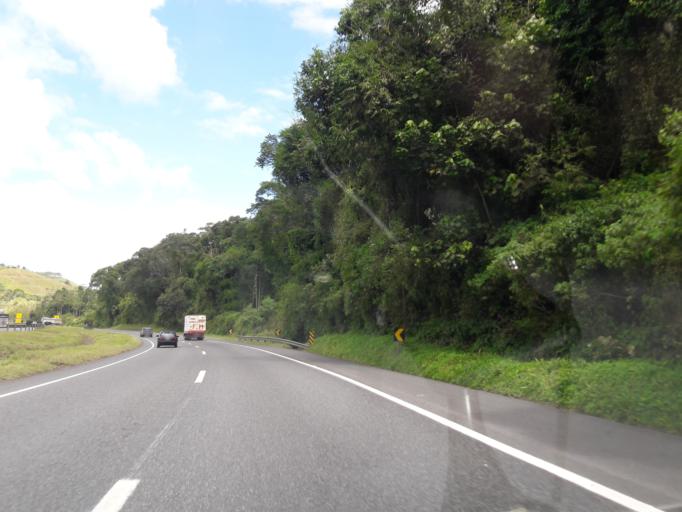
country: BR
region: Parana
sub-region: Antonina
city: Antonina
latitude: -25.0301
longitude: -48.5317
